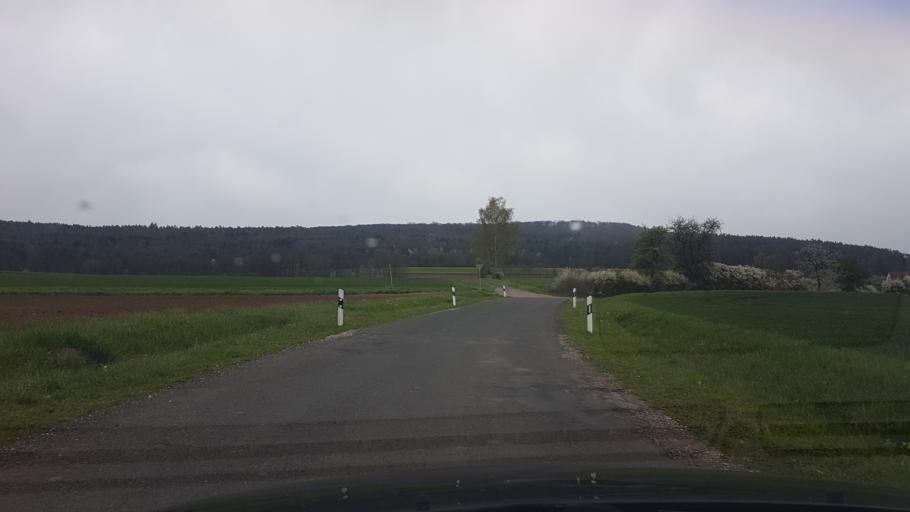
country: DE
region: Bavaria
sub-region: Upper Franconia
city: Reckendorf
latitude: 50.0374
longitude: 10.8413
